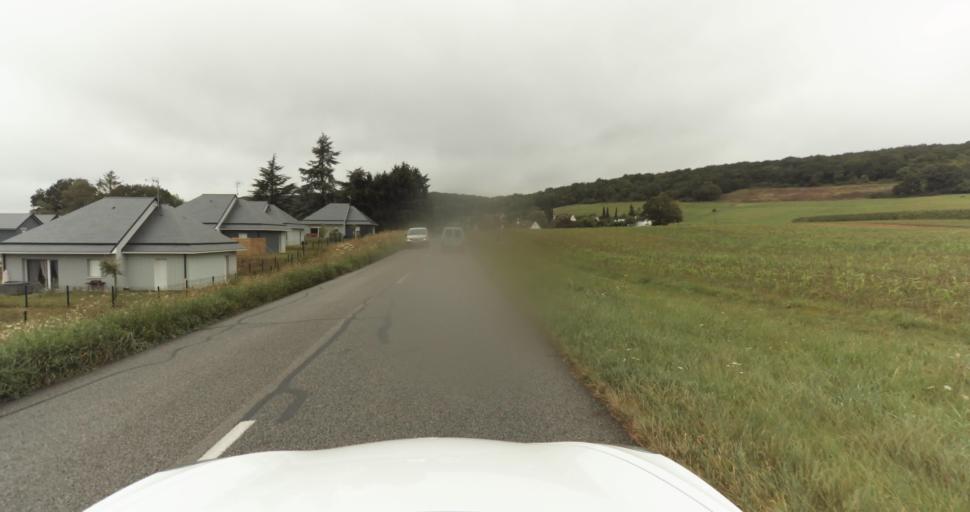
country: FR
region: Haute-Normandie
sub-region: Departement de l'Eure
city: Normanville
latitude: 49.0768
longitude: 1.1653
